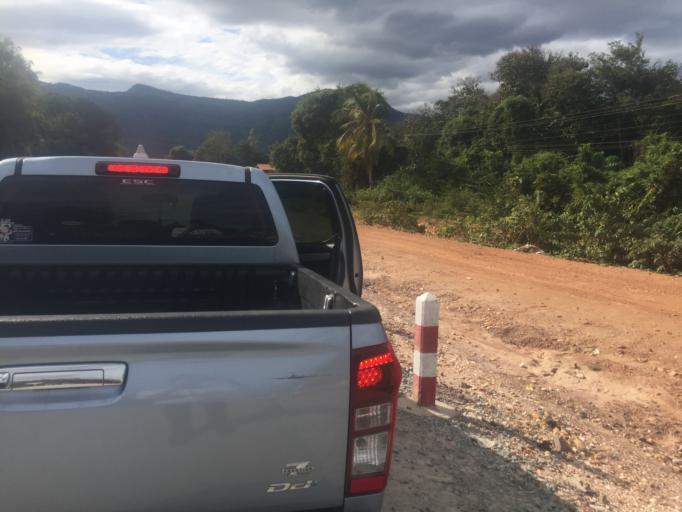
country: LA
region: Attapu
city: Attapu
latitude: 14.8076
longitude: 106.7657
